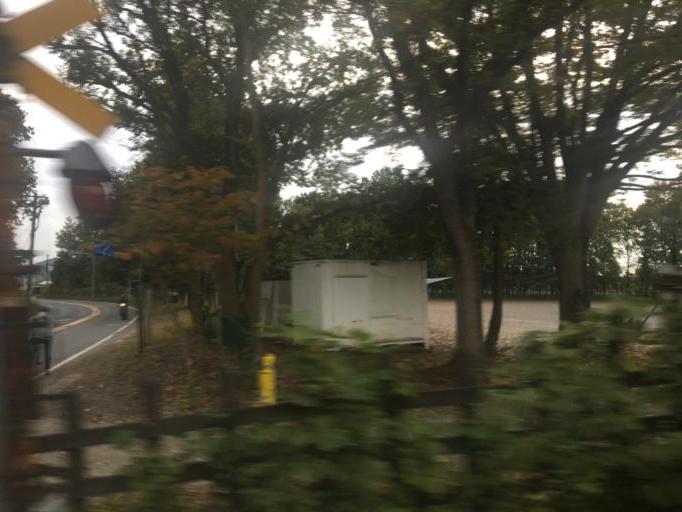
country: JP
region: Tokyo
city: Fussa
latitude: 35.7687
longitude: 139.3454
